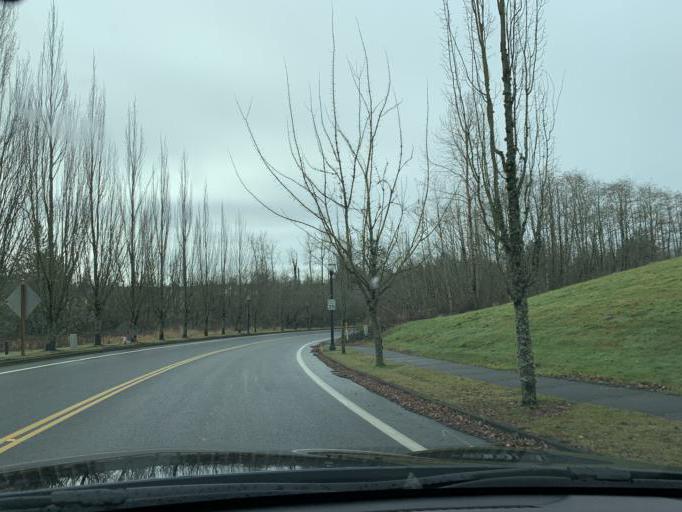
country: US
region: Washington
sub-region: Clark County
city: Camas
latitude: 45.5896
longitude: -122.4528
